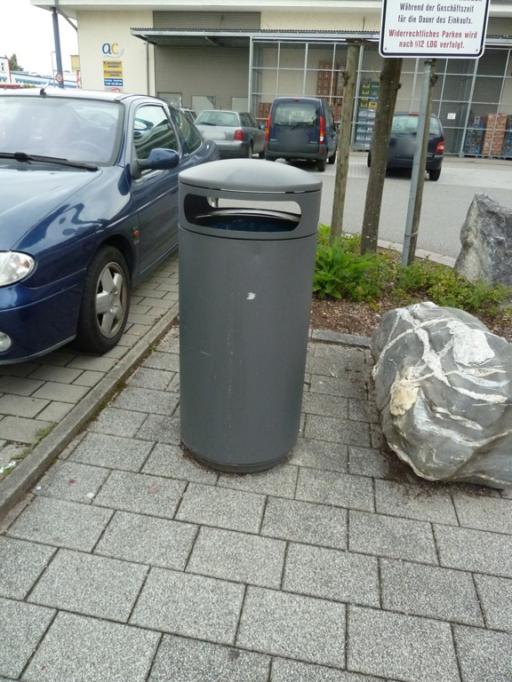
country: DE
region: Baden-Wuerttemberg
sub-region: Freiburg Region
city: Stockach
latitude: 47.8502
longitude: 9.0063
